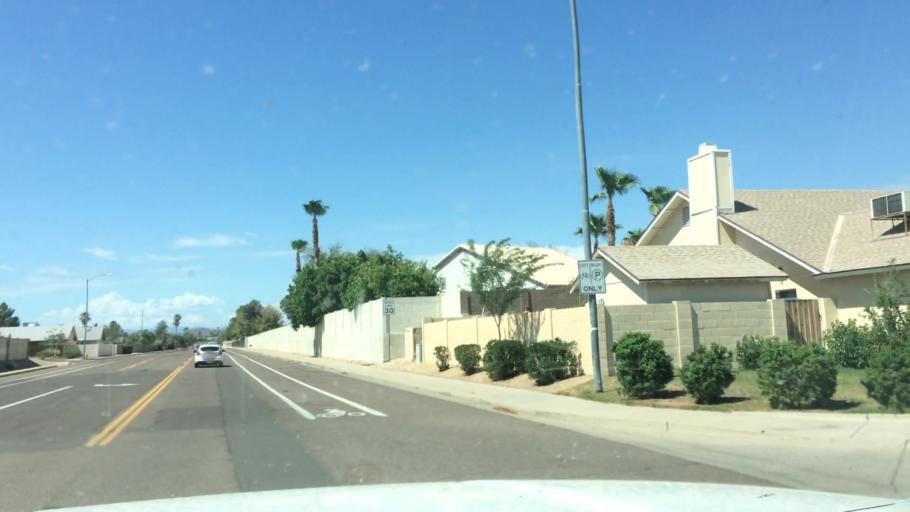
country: US
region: Arizona
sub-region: Maricopa County
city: Sun City
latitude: 33.6452
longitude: -112.2463
